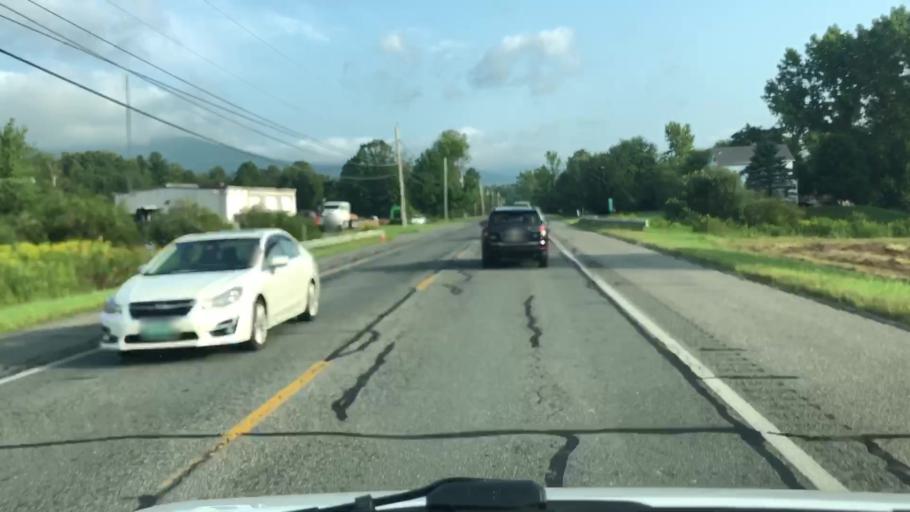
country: US
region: Massachusetts
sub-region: Berkshire County
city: Williamstown
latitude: 42.6499
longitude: -73.2370
